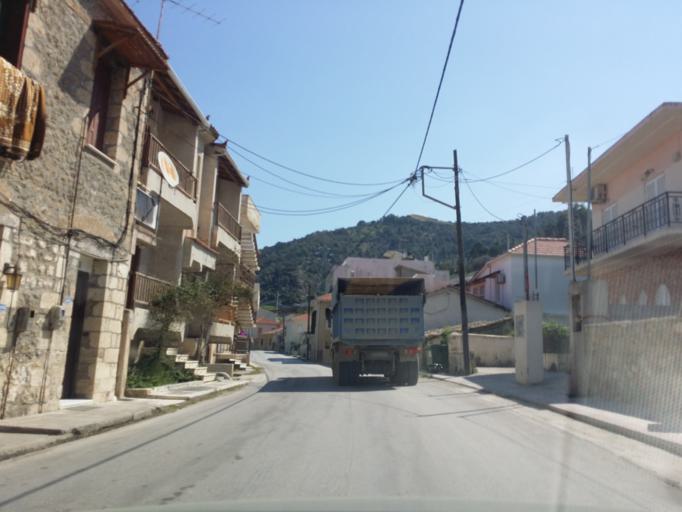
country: GR
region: West Greece
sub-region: Nomos Achaias
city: Aiyira
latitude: 38.1302
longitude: 22.4150
